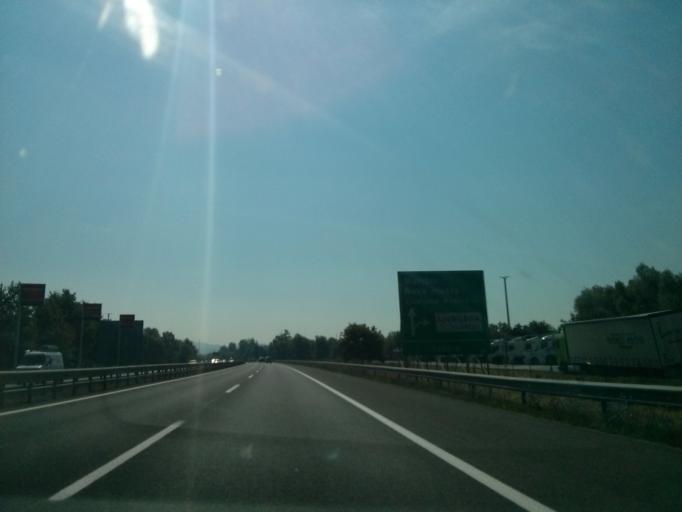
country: SI
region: Ljubljana
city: Ljubljana
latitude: 46.0289
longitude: 14.4804
